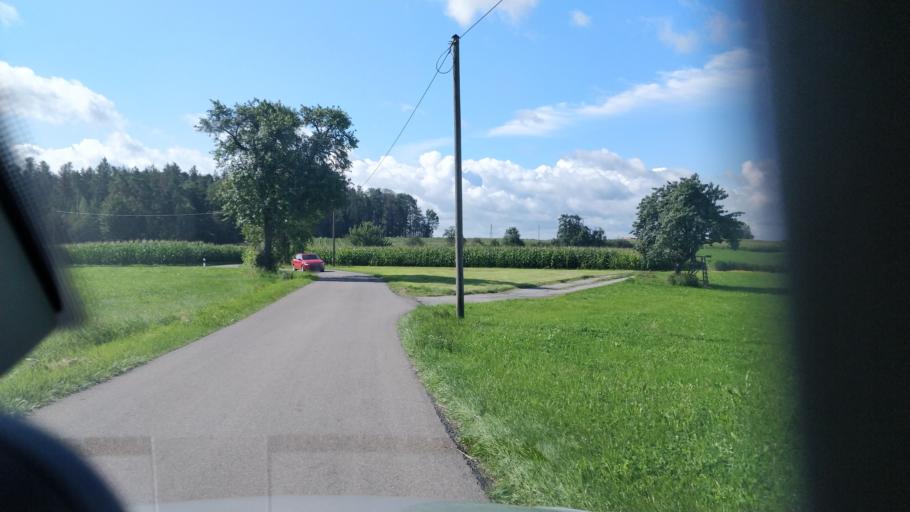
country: DE
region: Baden-Wuerttemberg
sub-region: Regierungsbezirk Stuttgart
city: Oberrot
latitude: 49.0048
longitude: 9.6498
